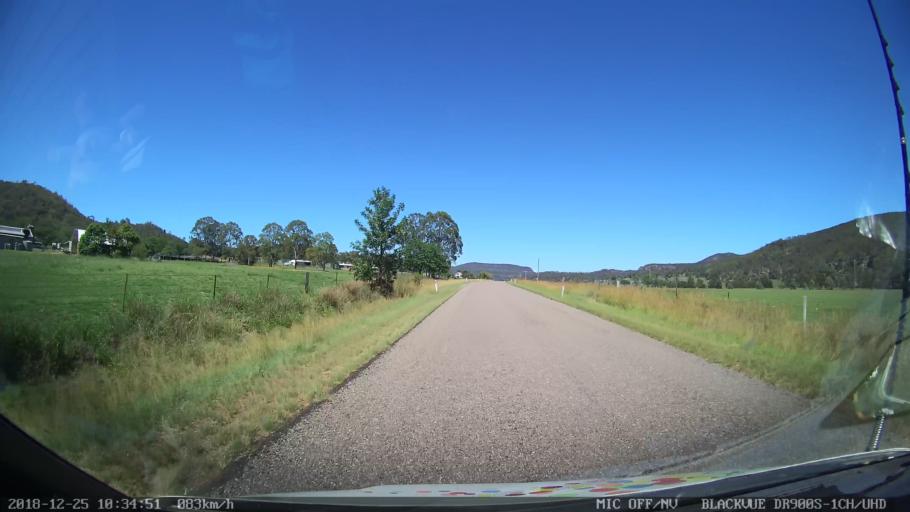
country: AU
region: New South Wales
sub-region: Upper Hunter Shire
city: Merriwa
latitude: -32.3943
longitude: 150.4027
